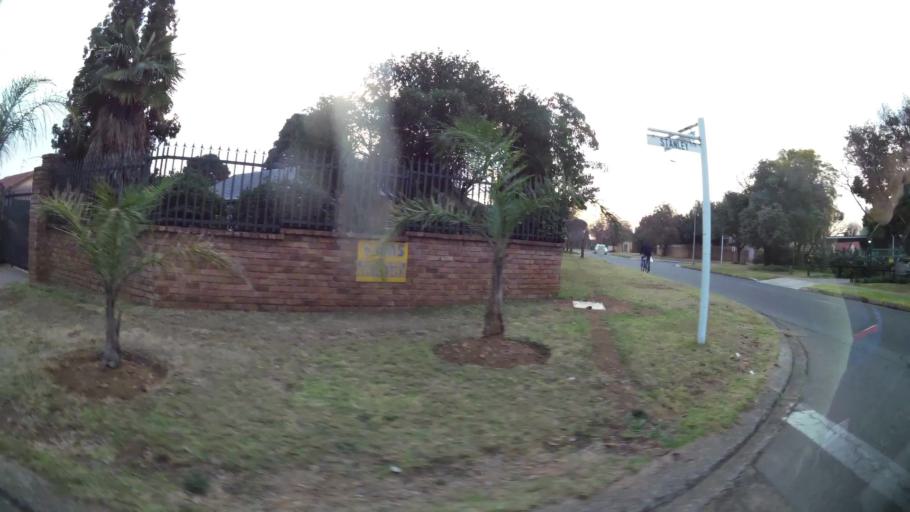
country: ZA
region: Gauteng
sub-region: Ekurhuleni Metropolitan Municipality
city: Benoni
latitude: -26.1715
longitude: 28.3046
